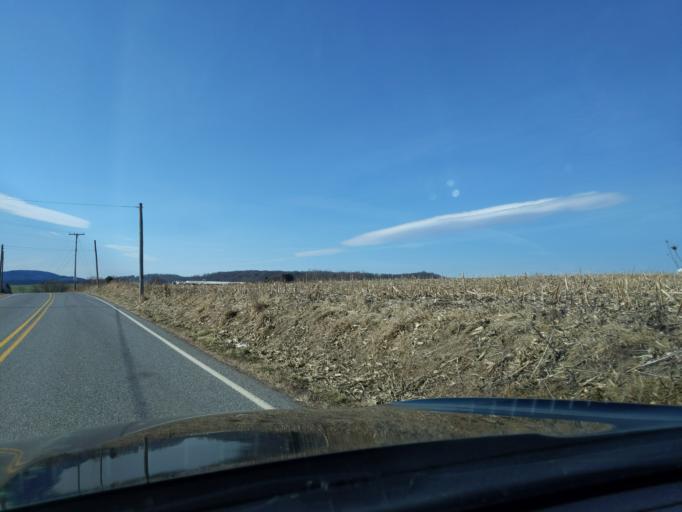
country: US
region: Pennsylvania
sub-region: Blair County
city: Martinsburg
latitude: 40.3127
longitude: -78.2795
